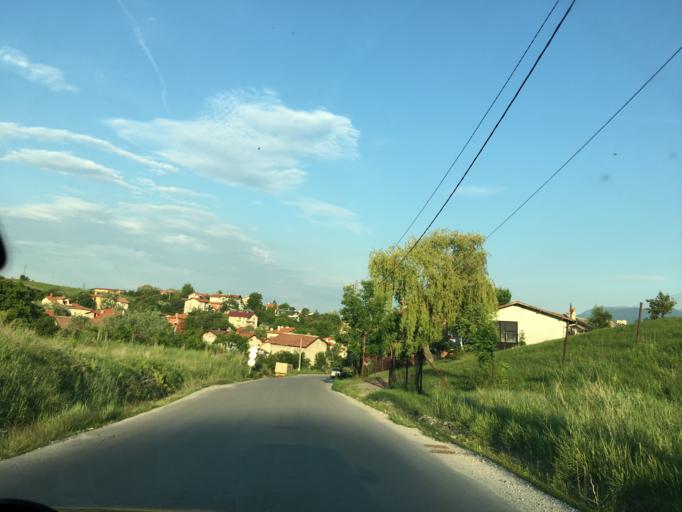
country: BG
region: Sofiya
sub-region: Obshtina Bozhurishte
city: Bozhurishte
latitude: 42.7227
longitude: 23.1277
